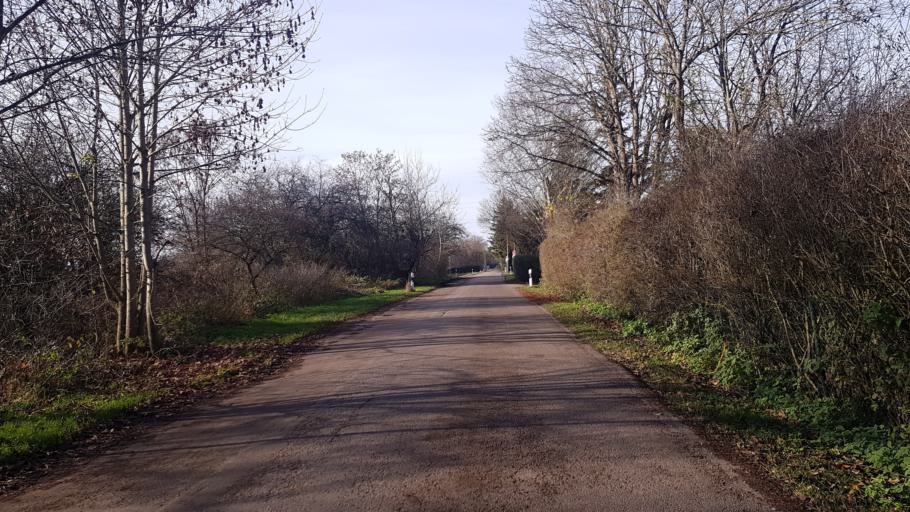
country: DE
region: Bavaria
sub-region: Upper Bavaria
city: Karlsfeld
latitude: 48.2426
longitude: 11.5120
